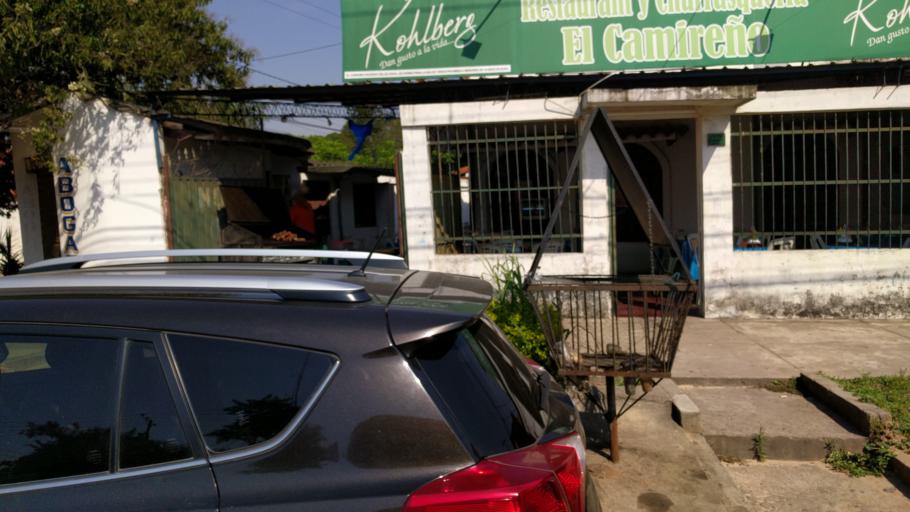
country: BO
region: Santa Cruz
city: Santa Cruz de la Sierra
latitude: -17.8140
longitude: -63.1818
